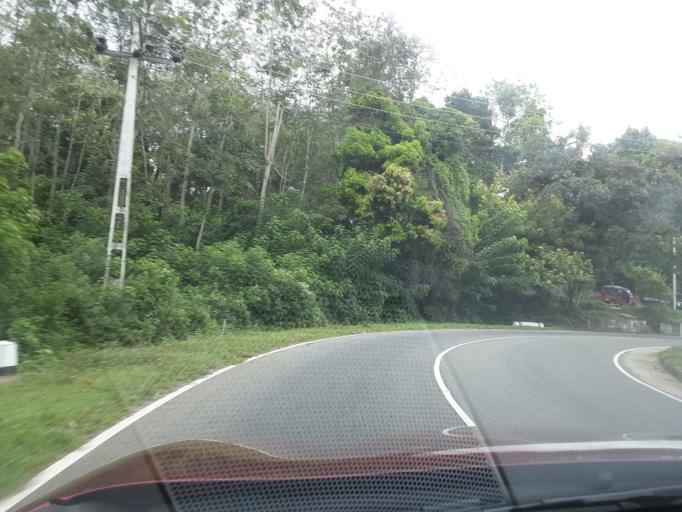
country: LK
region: Uva
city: Monaragala
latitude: 6.9006
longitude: 81.2151
